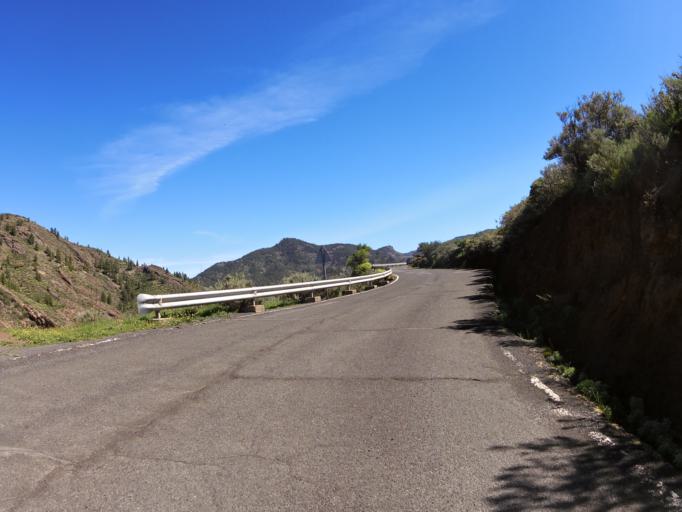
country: ES
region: Canary Islands
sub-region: Provincia de Las Palmas
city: Artenara
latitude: 28.0112
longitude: -15.6851
